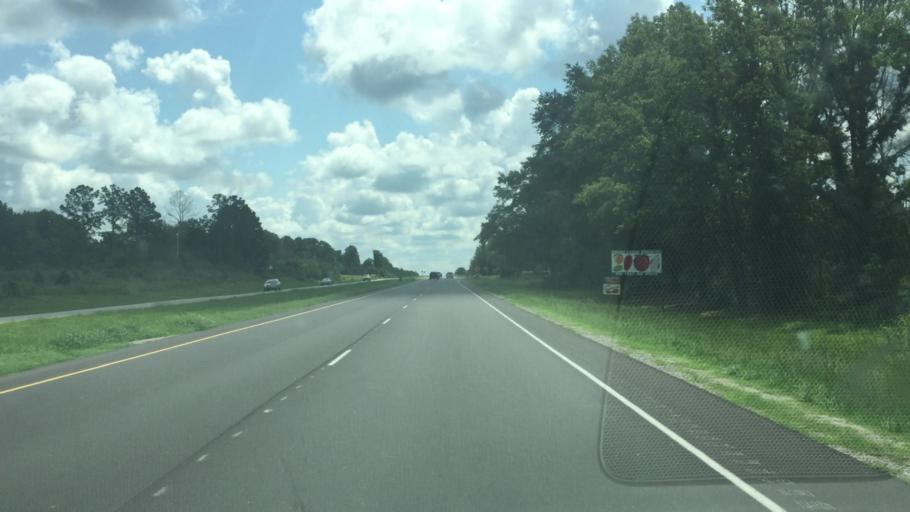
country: US
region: North Carolina
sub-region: Richmond County
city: Cordova
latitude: 34.9491
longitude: -79.9052
